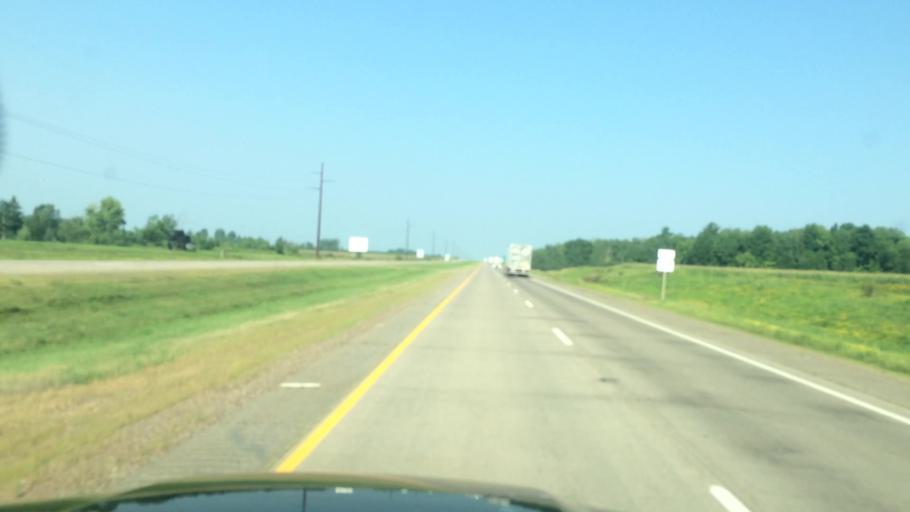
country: US
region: Wisconsin
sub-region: Marathon County
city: Edgar
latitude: 44.9445
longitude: -89.9733
